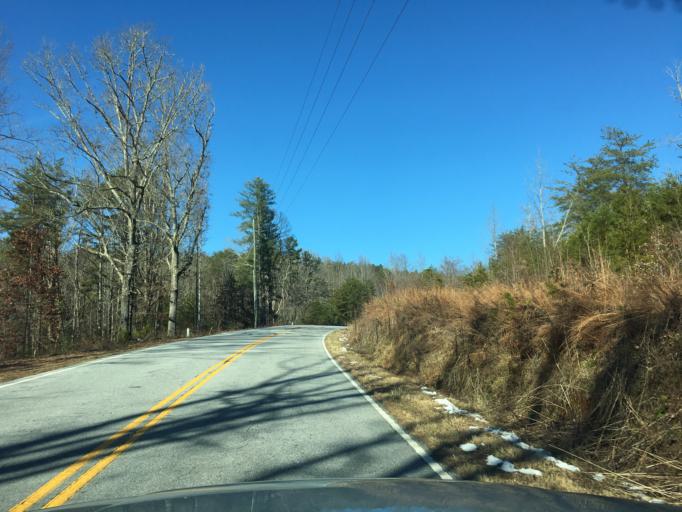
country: US
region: South Carolina
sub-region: Oconee County
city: Walhalla
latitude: 34.9151
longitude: -82.9852
